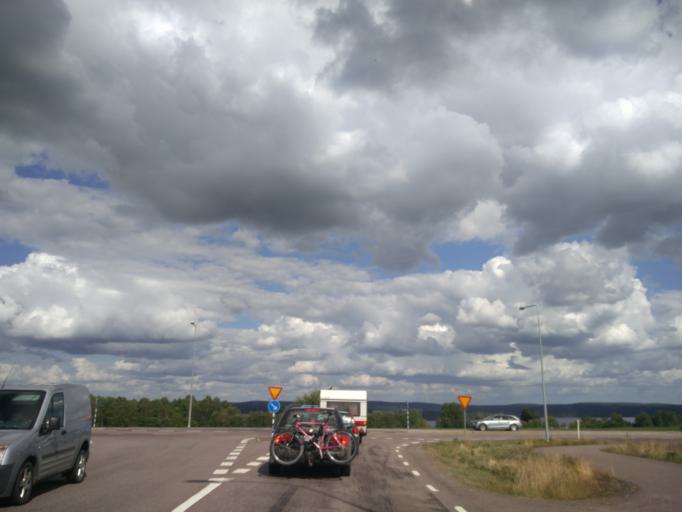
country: SE
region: Vaermland
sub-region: Sunne Kommun
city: Sunne
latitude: 59.7355
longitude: 13.1309
